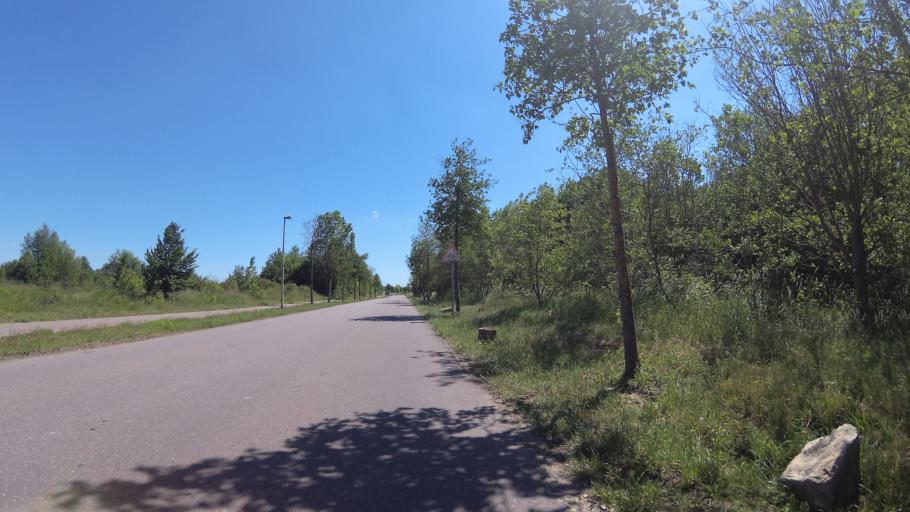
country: DE
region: Saarland
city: Saarwellingen
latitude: 49.3535
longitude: 6.7876
